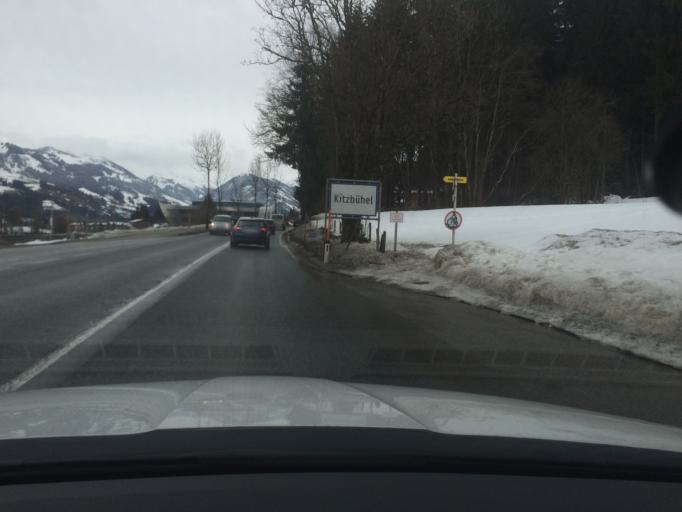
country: AT
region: Tyrol
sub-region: Politischer Bezirk Kitzbuhel
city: Kitzbuhel
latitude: 47.4533
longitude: 12.3701
